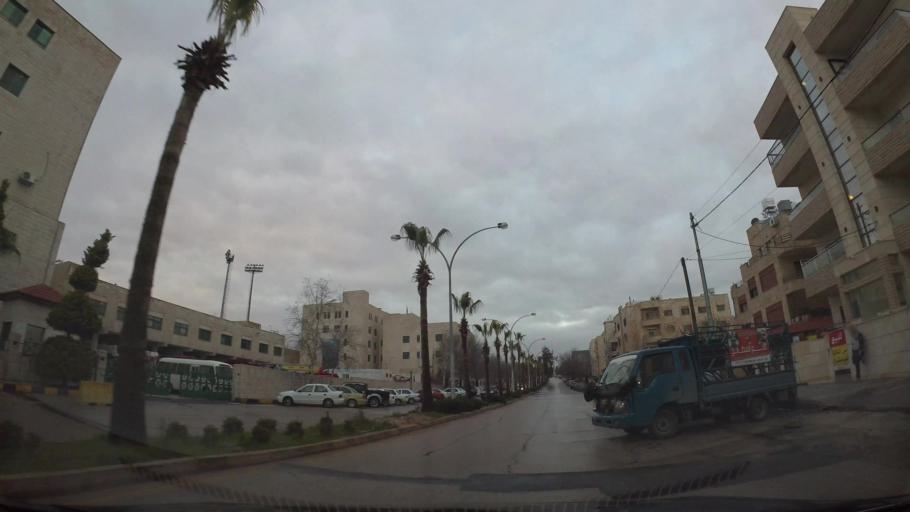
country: JO
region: Amman
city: Amman
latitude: 31.9802
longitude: 35.9108
